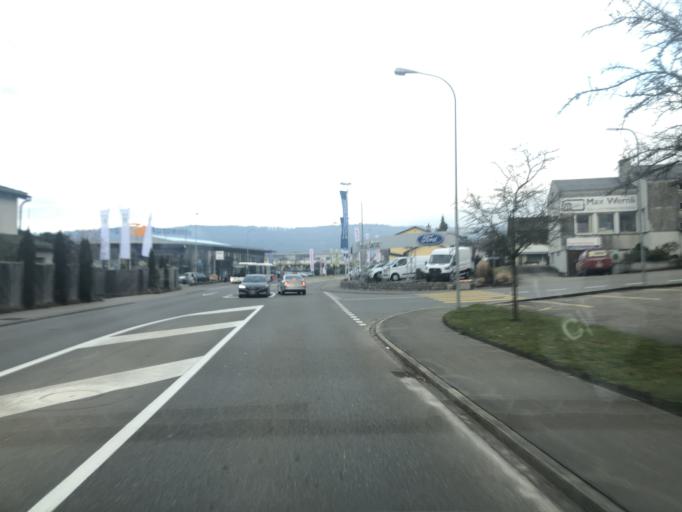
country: CH
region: Aargau
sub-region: Bezirk Baden
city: Gebenstorf
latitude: 47.4887
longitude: 8.2452
